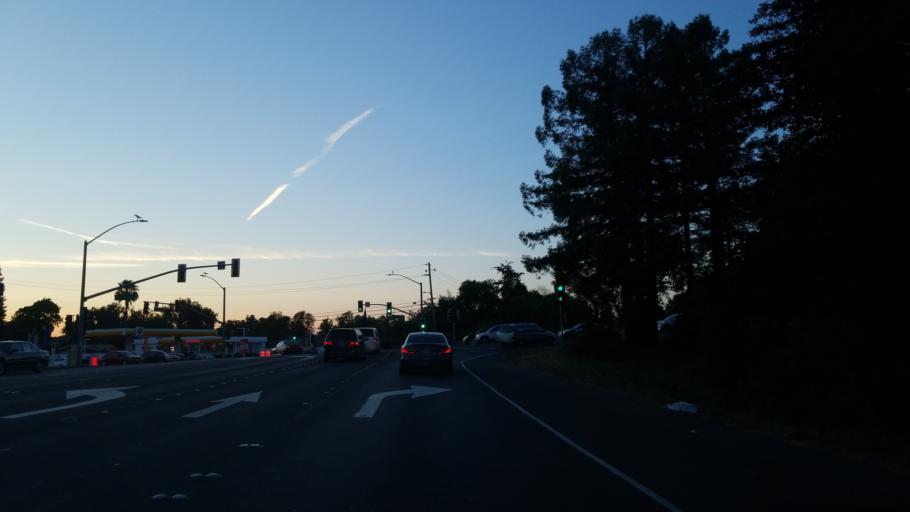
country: US
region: California
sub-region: Sonoma County
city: Roseland
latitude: 38.4137
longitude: -122.7172
